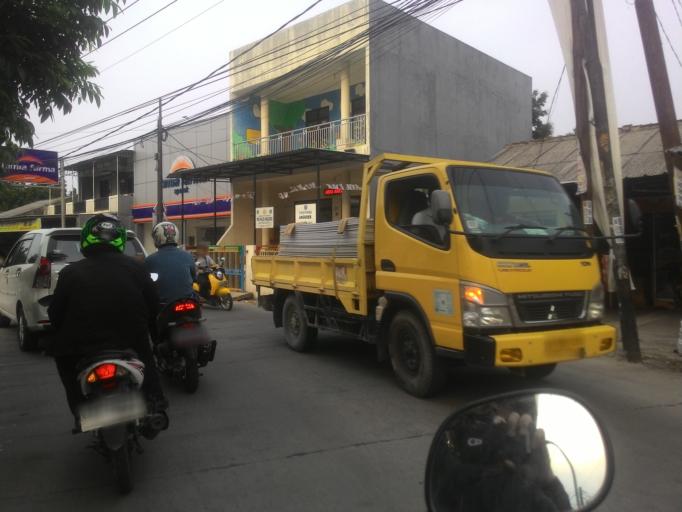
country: ID
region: West Java
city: Depok
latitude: -6.3622
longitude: 106.8163
